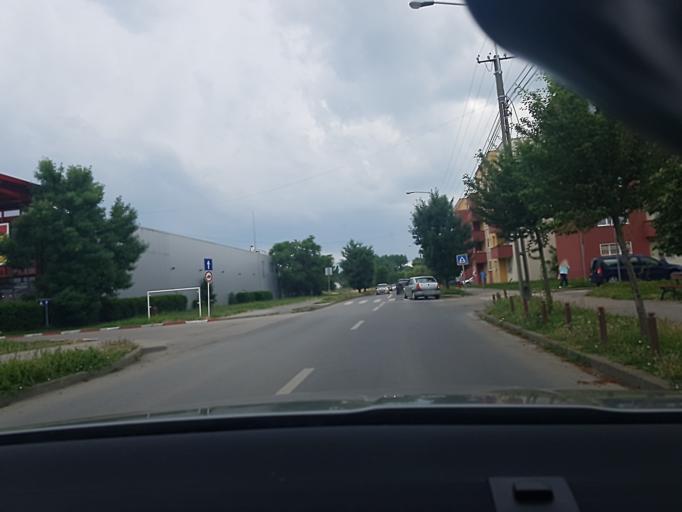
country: RO
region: Timis
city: Timisoara
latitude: 45.7370
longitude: 21.2443
